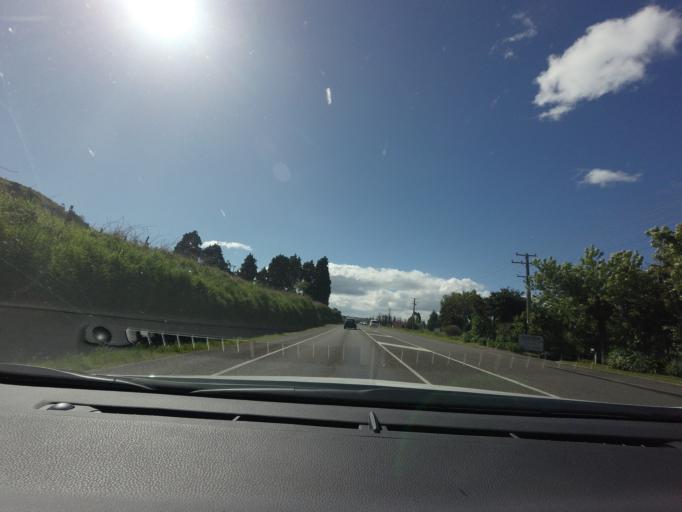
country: NZ
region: Bay of Plenty
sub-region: Rotorua District
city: Rotorua
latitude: -38.0946
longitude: 176.2174
